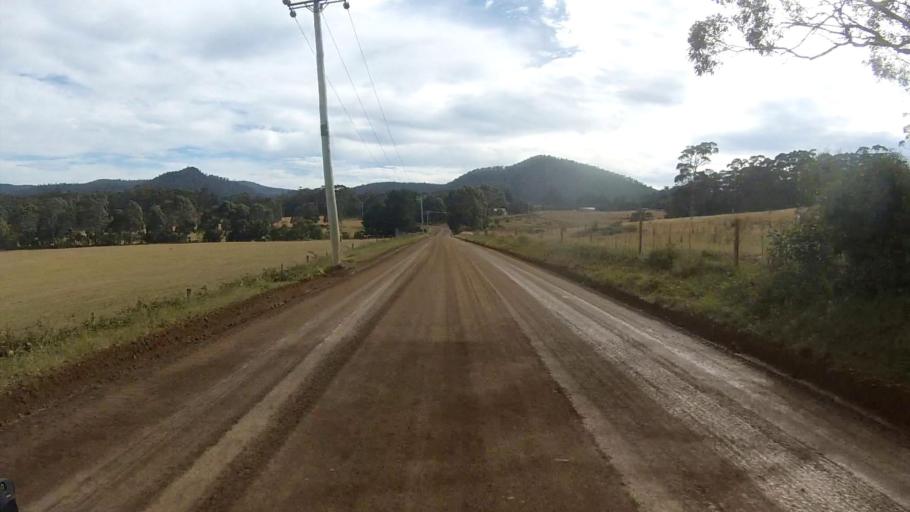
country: AU
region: Tasmania
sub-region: Sorell
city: Sorell
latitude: -42.7829
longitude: 147.8085
